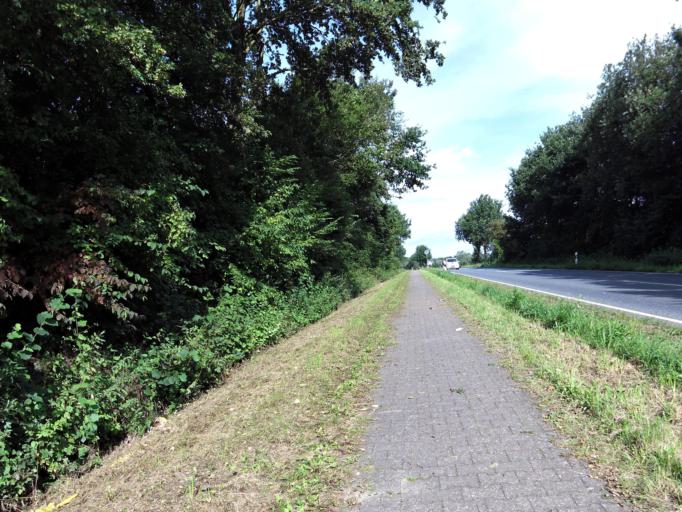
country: DE
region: North Rhine-Westphalia
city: Siersdorf
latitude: 50.8513
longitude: 6.2215
